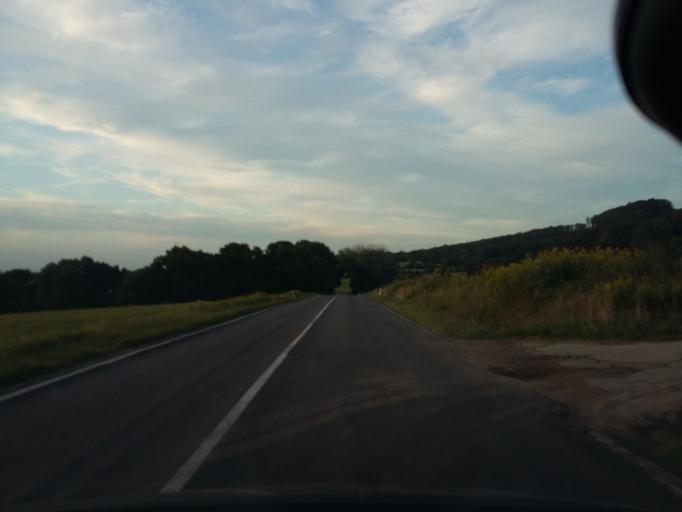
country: SK
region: Bratislavsky
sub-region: Okres Malacky
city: Malacky
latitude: 48.3815
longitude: 17.1520
